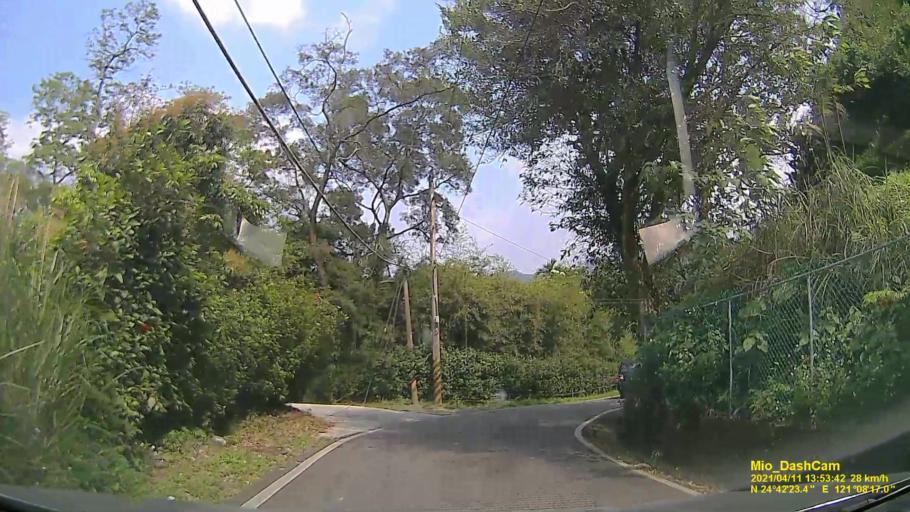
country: TW
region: Taiwan
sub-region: Hsinchu
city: Zhubei
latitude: 24.7065
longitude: 121.1382
